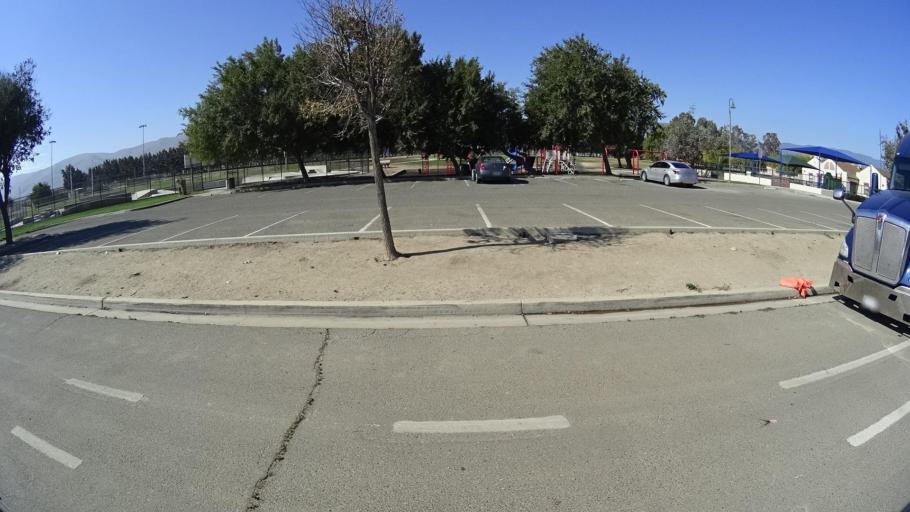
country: US
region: California
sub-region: Monterey County
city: Greenfield
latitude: 36.3117
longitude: -121.2573
